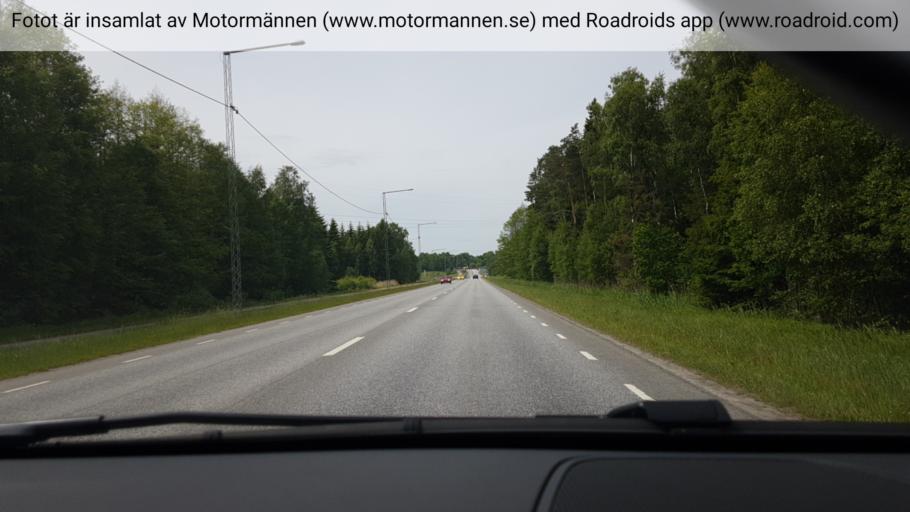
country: SE
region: Stockholm
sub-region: Haninge Kommun
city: Jordbro
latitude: 59.1222
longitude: 18.1255
